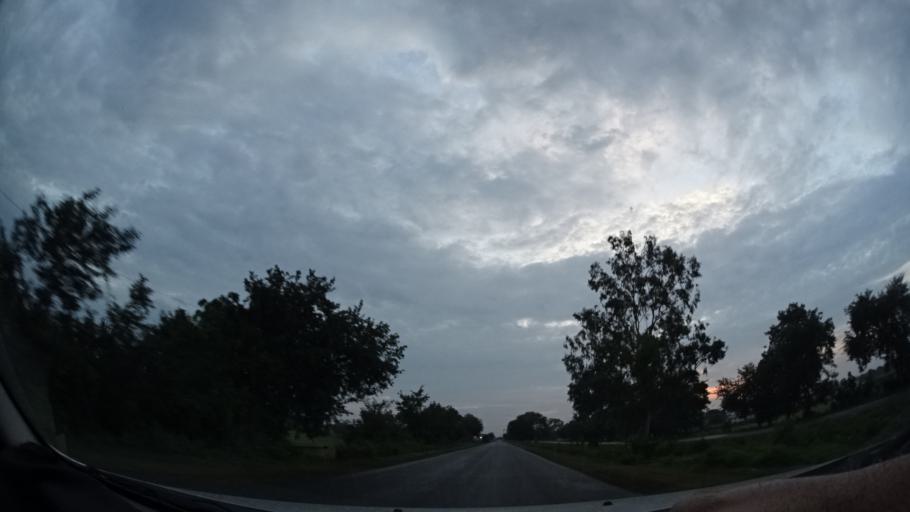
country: IN
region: Madhya Pradesh
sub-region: Dewas
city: Dewas
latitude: 22.9777
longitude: 76.1706
